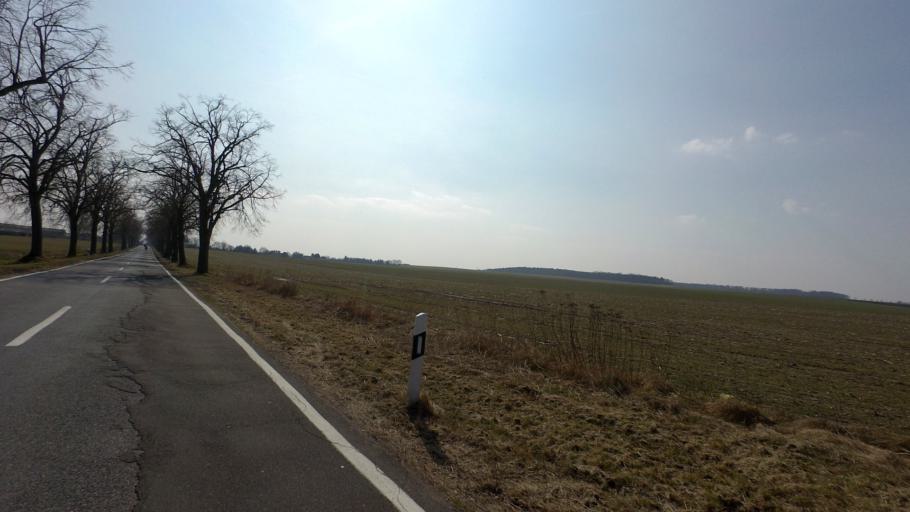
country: DE
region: Brandenburg
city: Gross Kreutz
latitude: 52.4251
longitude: 12.7888
